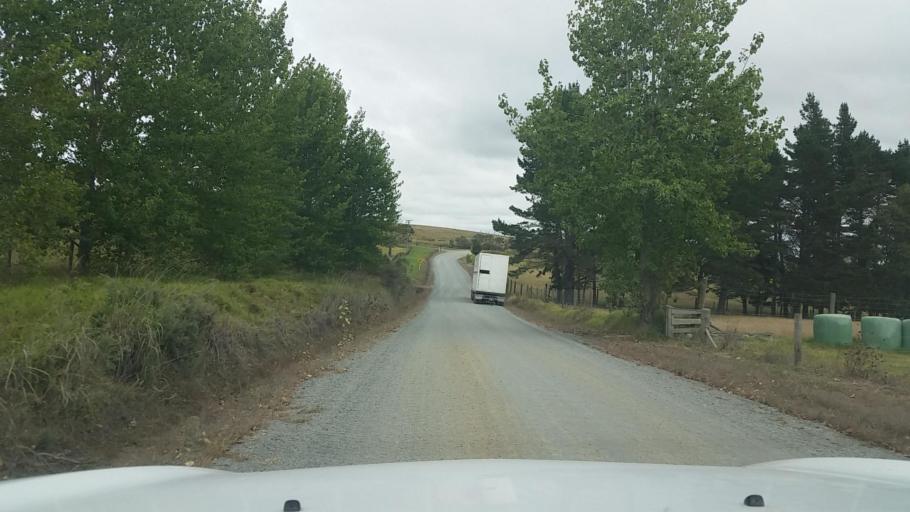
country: NZ
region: Northland
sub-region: Whangarei
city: Maungatapere
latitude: -35.6721
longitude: 174.1623
